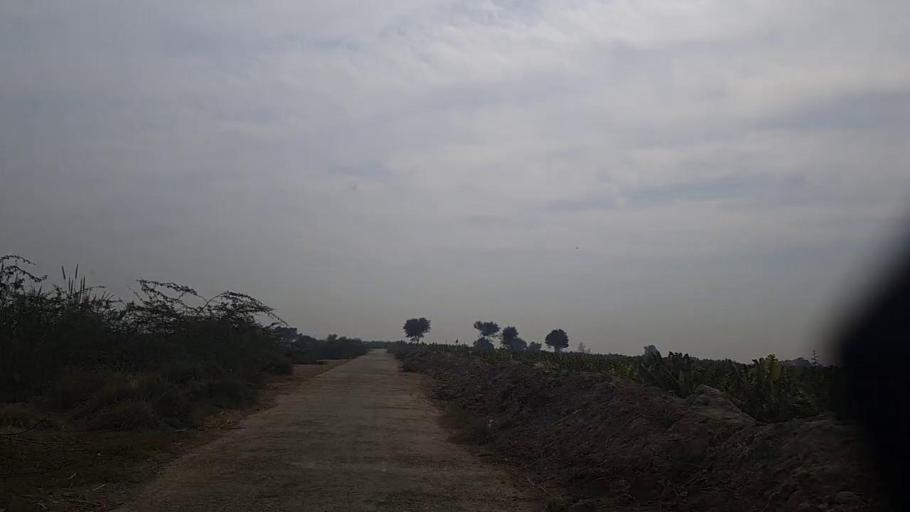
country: PK
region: Sindh
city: Sakrand
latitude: 26.2431
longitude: 68.2955
